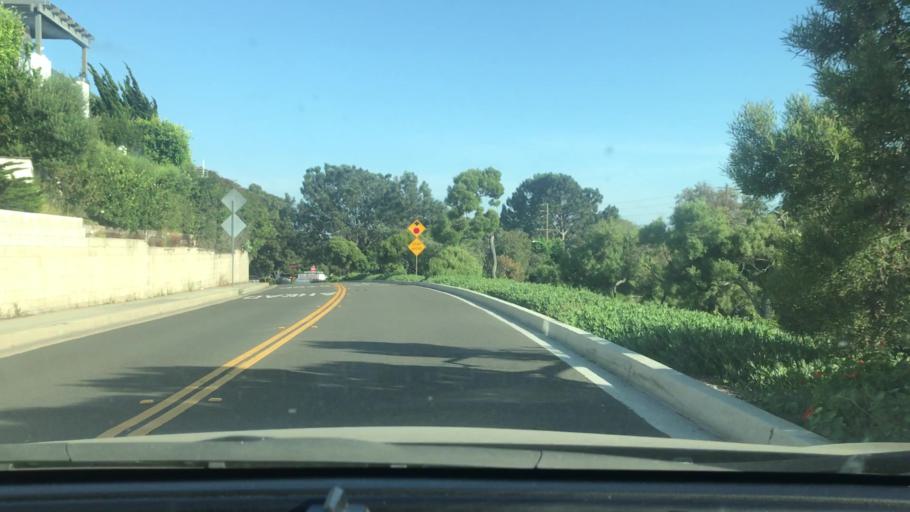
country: US
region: California
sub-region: Los Angeles County
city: Hermosa Beach
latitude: 33.8755
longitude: -118.4012
